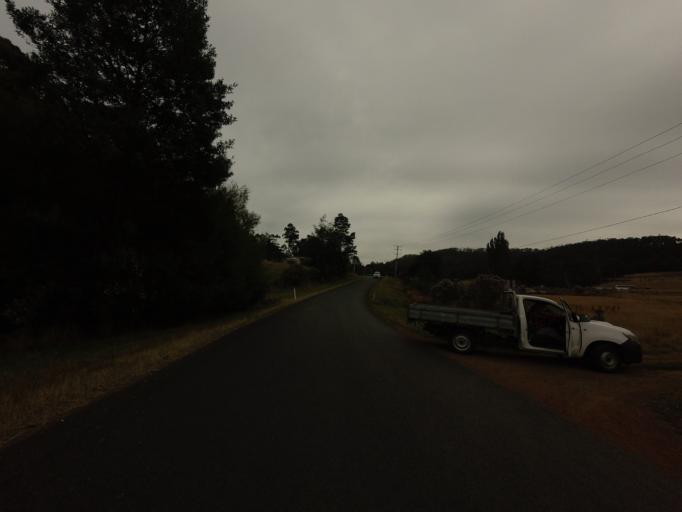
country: AU
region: Tasmania
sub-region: Sorell
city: Sorell
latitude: -42.5280
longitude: 147.5626
